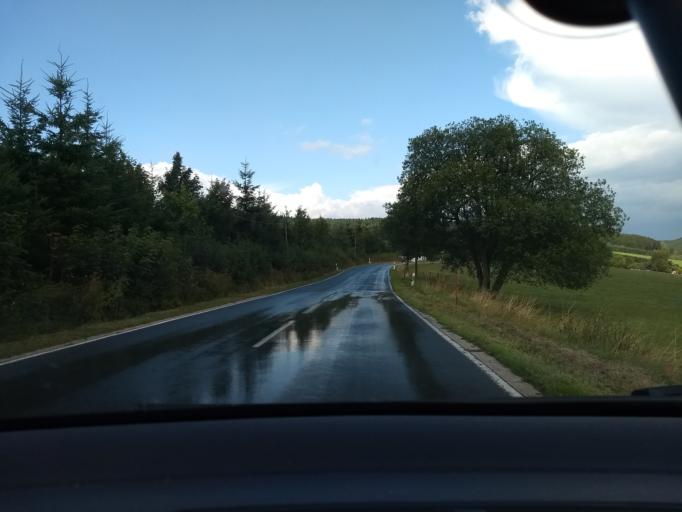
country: DE
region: North Rhine-Westphalia
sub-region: Regierungsbezirk Arnsberg
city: Finnentrop
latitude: 51.2209
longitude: 8.0267
